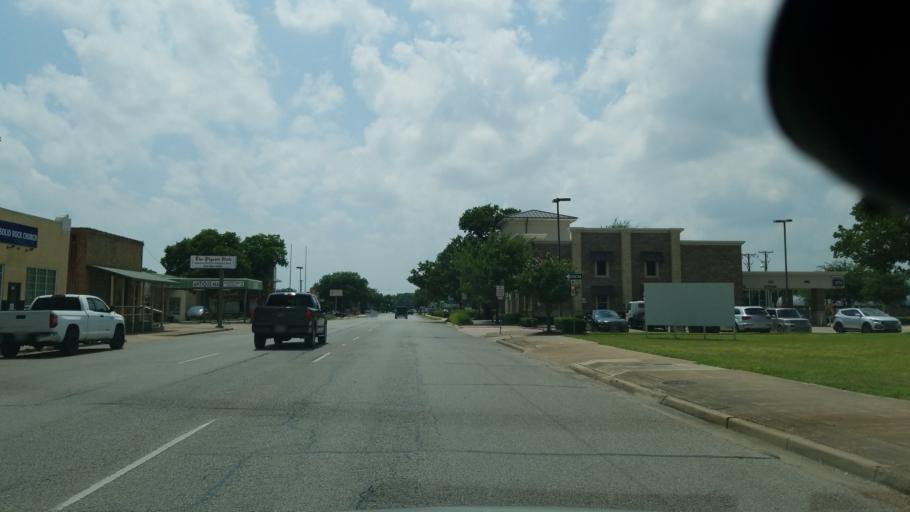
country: US
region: Texas
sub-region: Dallas County
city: Irving
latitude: 32.8139
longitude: -96.9465
